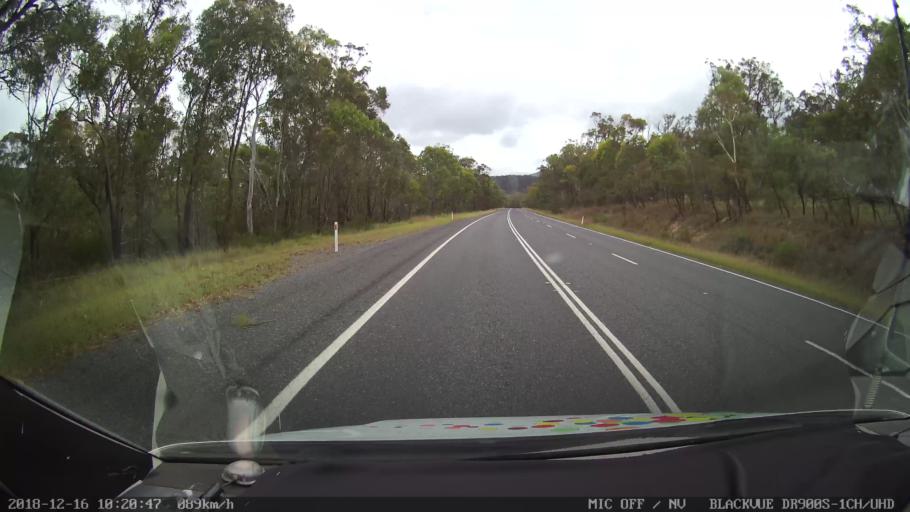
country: AU
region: New South Wales
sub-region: Tenterfield Municipality
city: Carrolls Creek
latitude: -29.2156
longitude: 152.0102
